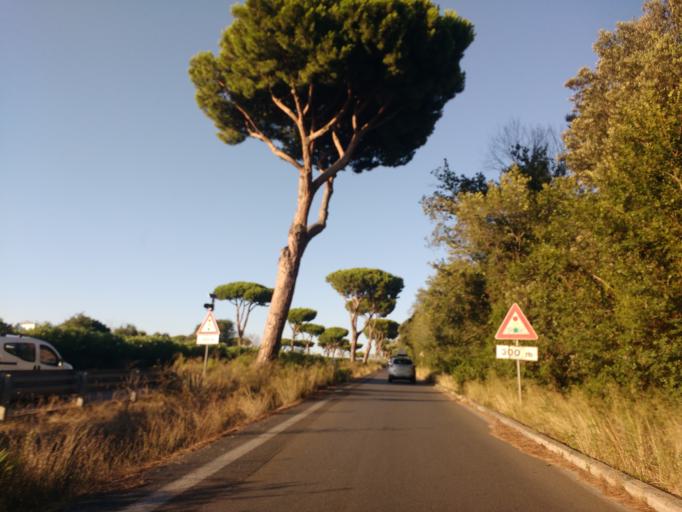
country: IT
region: Latium
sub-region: Citta metropolitana di Roma Capitale
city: Vitinia
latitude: 41.7630
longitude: 12.3806
